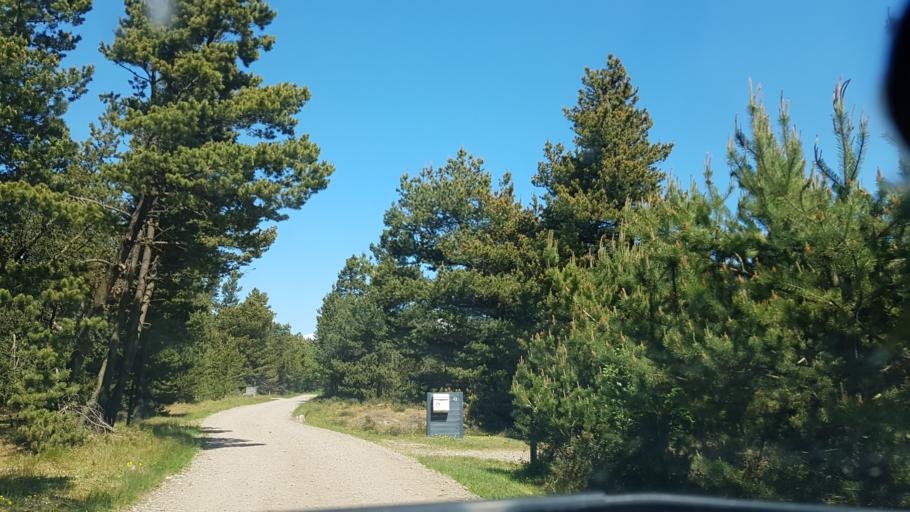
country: DE
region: Schleswig-Holstein
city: List
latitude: 55.1071
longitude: 8.5477
